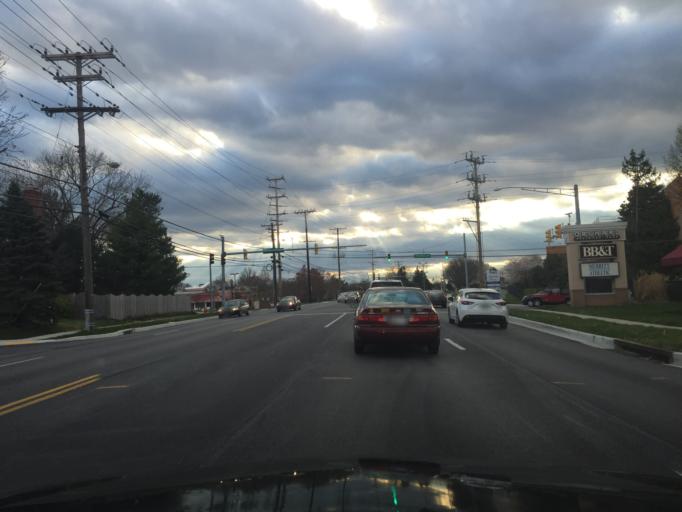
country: US
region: Maryland
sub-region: Baltimore County
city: Towson
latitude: 39.3959
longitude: -76.5737
